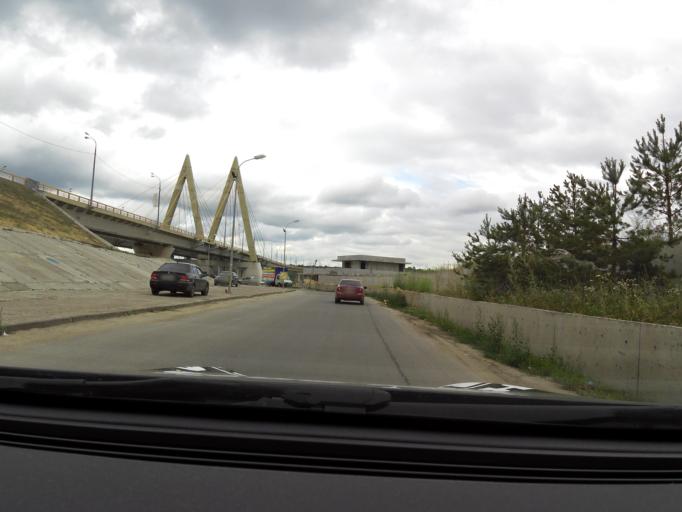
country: RU
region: Tatarstan
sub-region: Gorod Kazan'
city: Kazan
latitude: 55.8070
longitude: 49.1398
